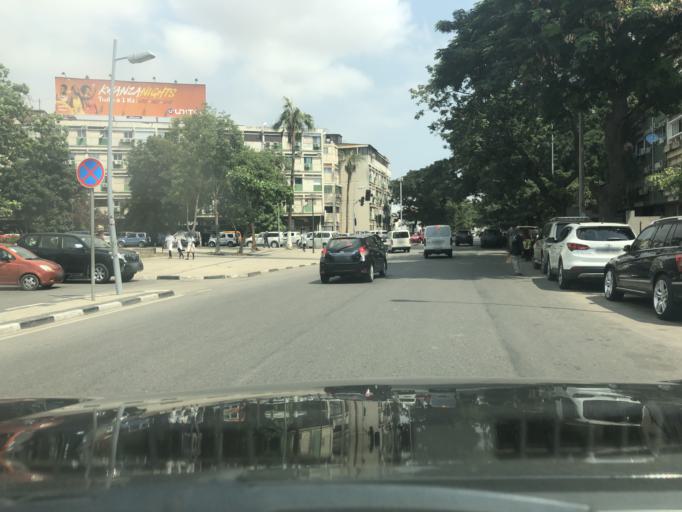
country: AO
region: Luanda
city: Luanda
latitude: -8.8246
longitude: 13.2380
